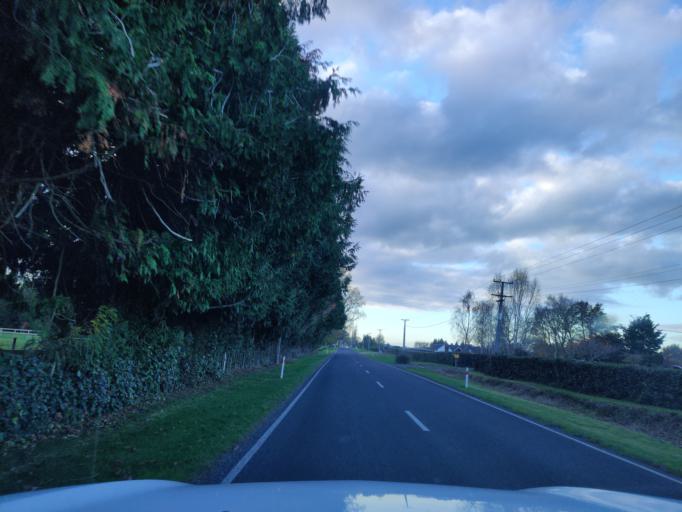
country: NZ
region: Waikato
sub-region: Waipa District
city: Cambridge
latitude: -37.8500
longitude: 175.4390
